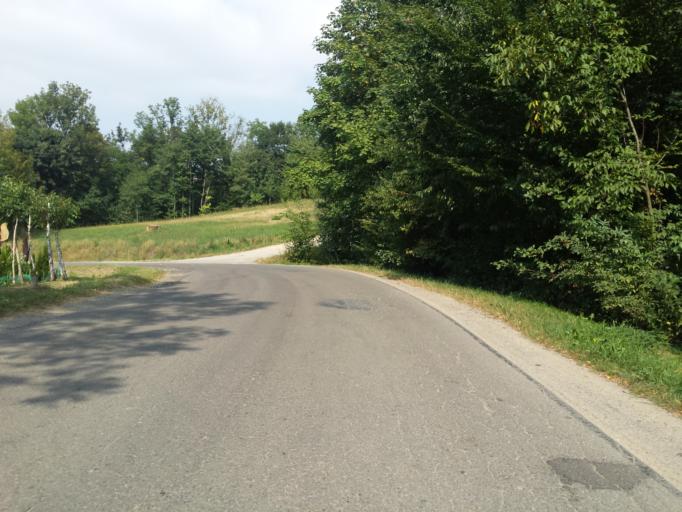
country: PL
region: Subcarpathian Voivodeship
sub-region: Powiat rzeszowski
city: Blazowa
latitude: 49.8475
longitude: 22.1422
